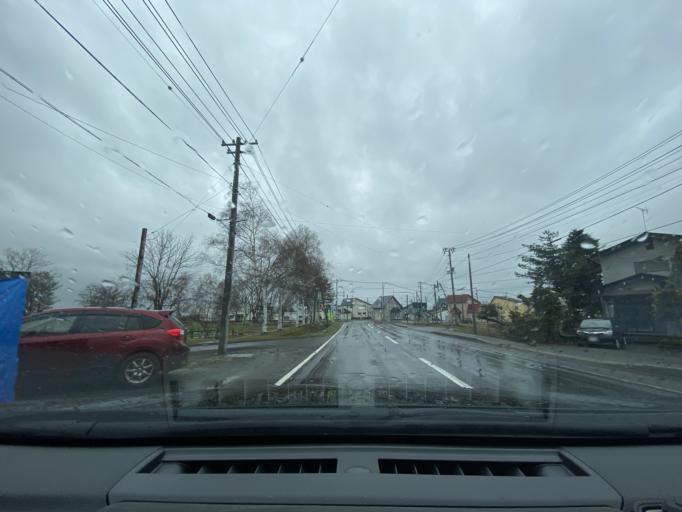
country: JP
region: Hokkaido
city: Fukagawa
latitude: 43.8095
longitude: 141.9471
